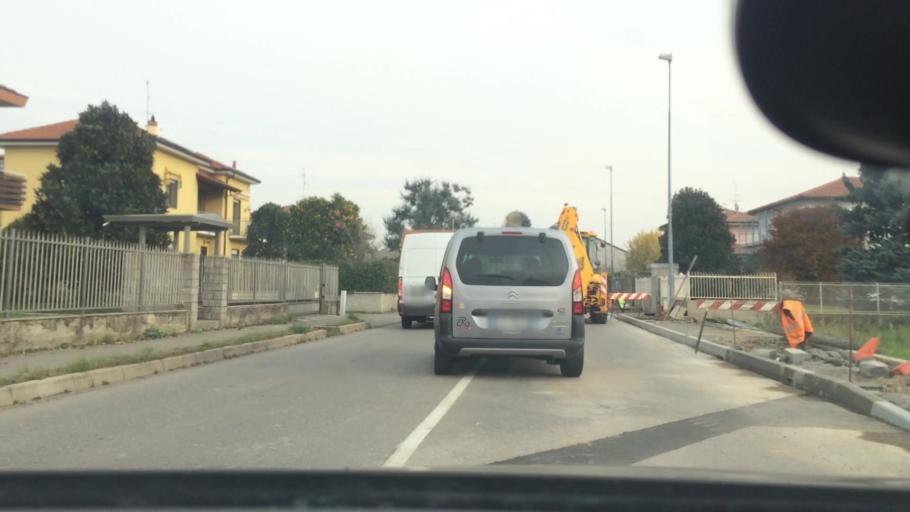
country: IT
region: Lombardy
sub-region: Provincia di Como
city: Rovello Porro
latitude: 45.6524
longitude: 9.0309
